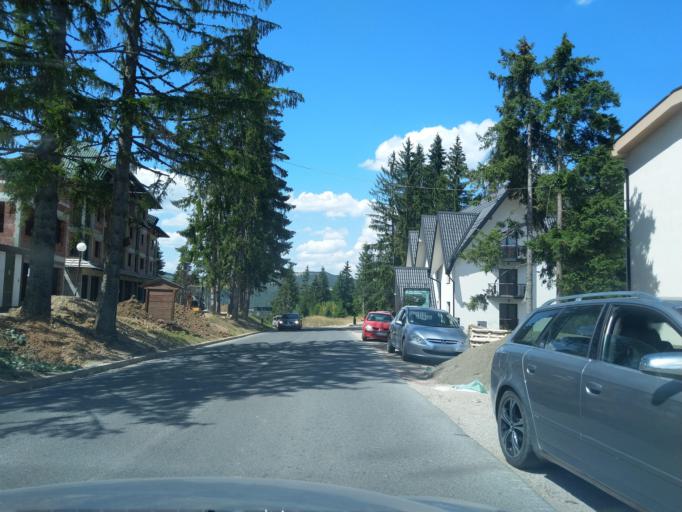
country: RS
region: Central Serbia
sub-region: Zlatiborski Okrug
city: Nova Varos
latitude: 43.4483
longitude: 19.8189
